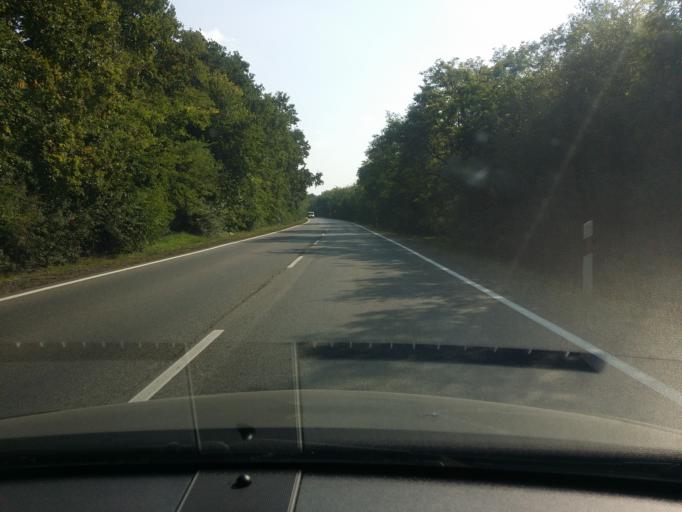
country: HU
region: Fejer
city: dunaujvaros
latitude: 46.9456
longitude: 18.9146
